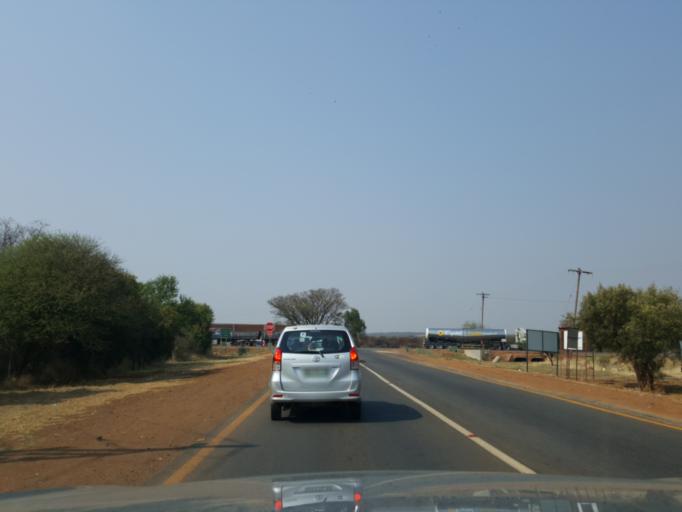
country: ZA
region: North-West
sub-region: Ngaka Modiri Molema District Municipality
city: Zeerust
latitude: -25.5034
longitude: 25.9836
